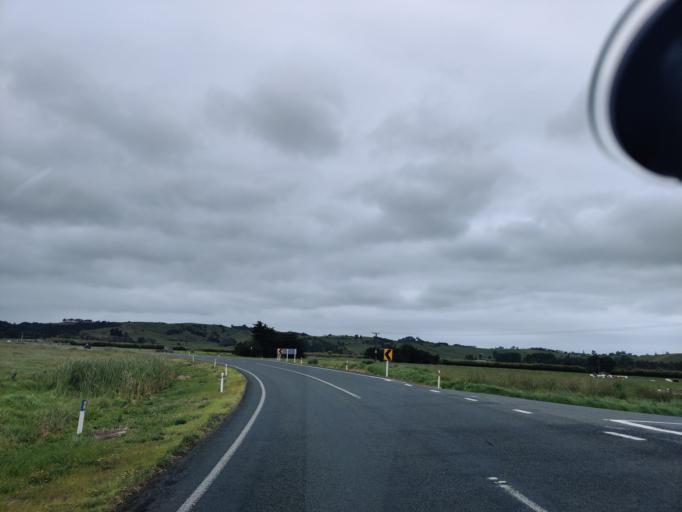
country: NZ
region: Northland
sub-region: Kaipara District
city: Dargaville
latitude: -36.1229
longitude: 174.0953
